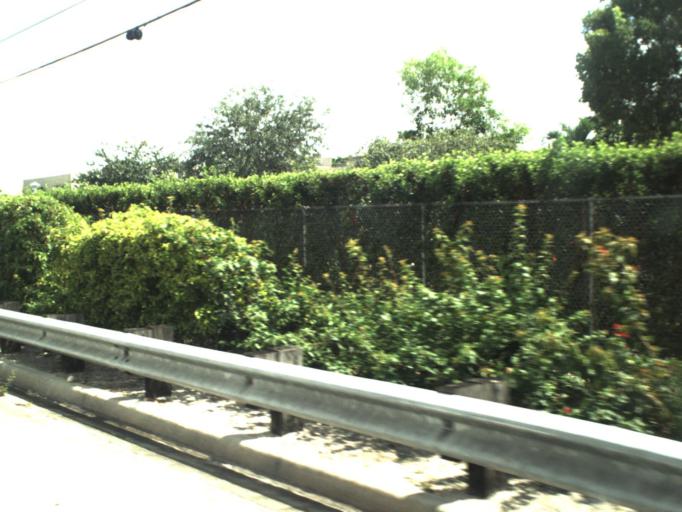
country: US
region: Florida
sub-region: Broward County
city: Sunshine Ranches
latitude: 26.0168
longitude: -80.3120
